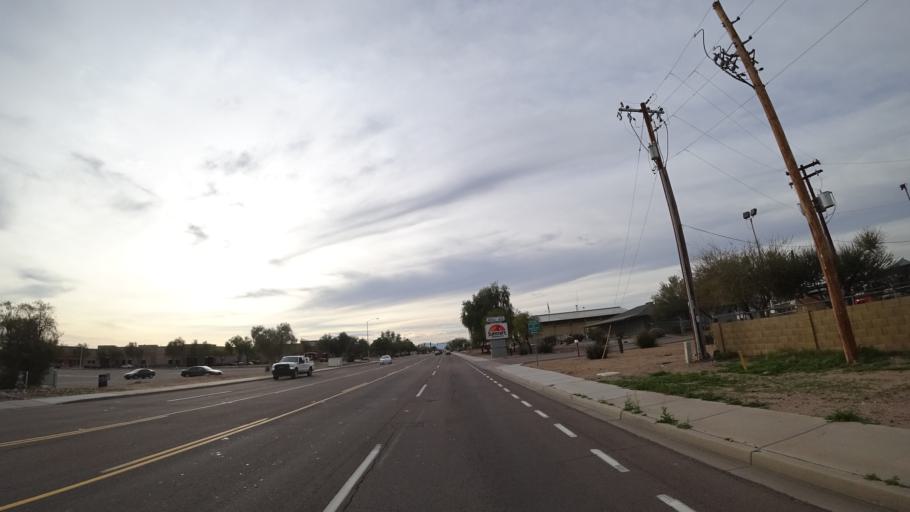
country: US
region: Arizona
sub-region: Maricopa County
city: Peoria
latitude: 33.5669
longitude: -112.2262
